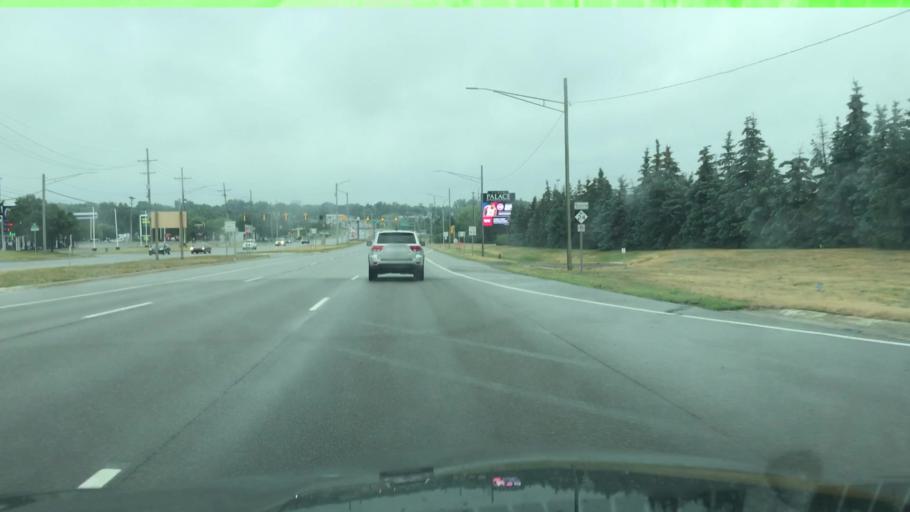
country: US
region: Michigan
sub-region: Oakland County
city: Auburn Hills
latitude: 42.7004
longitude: -83.2425
